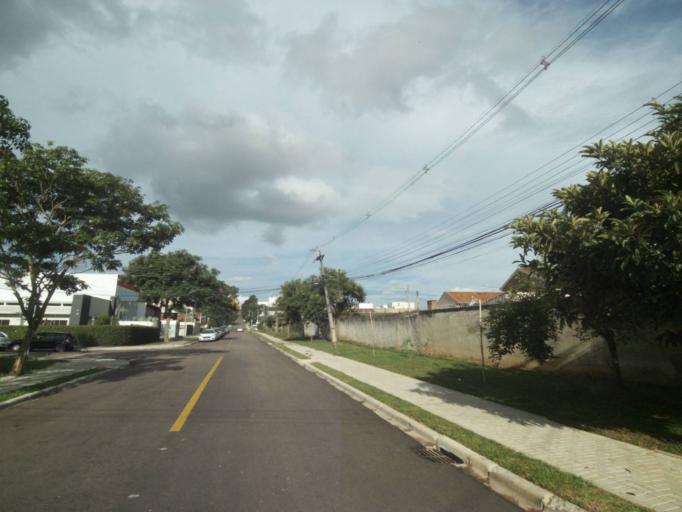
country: BR
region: Parana
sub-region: Curitiba
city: Curitiba
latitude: -25.4438
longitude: -49.3148
